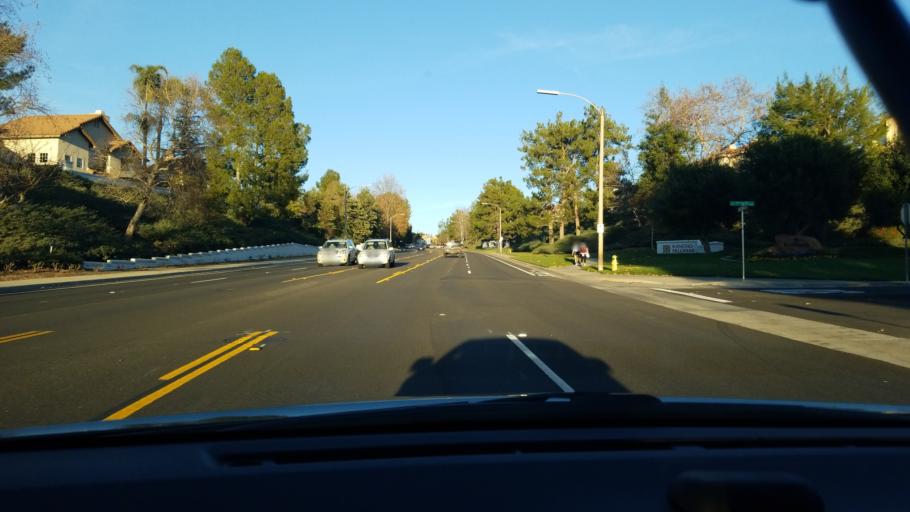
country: US
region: California
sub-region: Riverside County
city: Temecula
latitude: 33.4658
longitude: -117.1007
